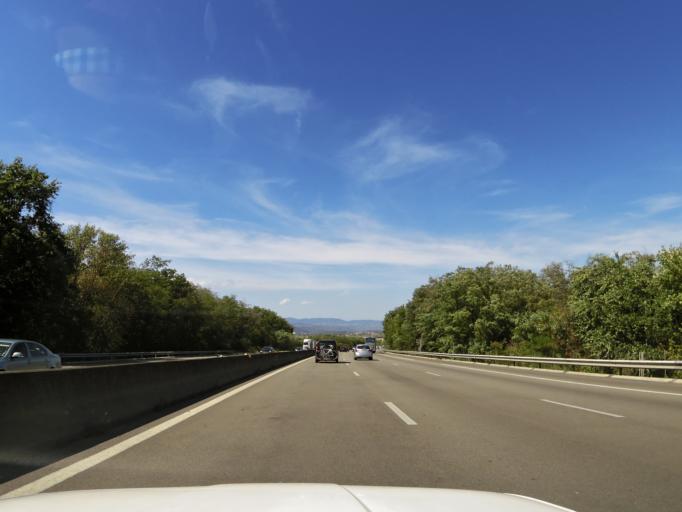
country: FR
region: Rhone-Alpes
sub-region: Departement de la Drome
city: Beausemblant
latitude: 45.2305
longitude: 4.8502
